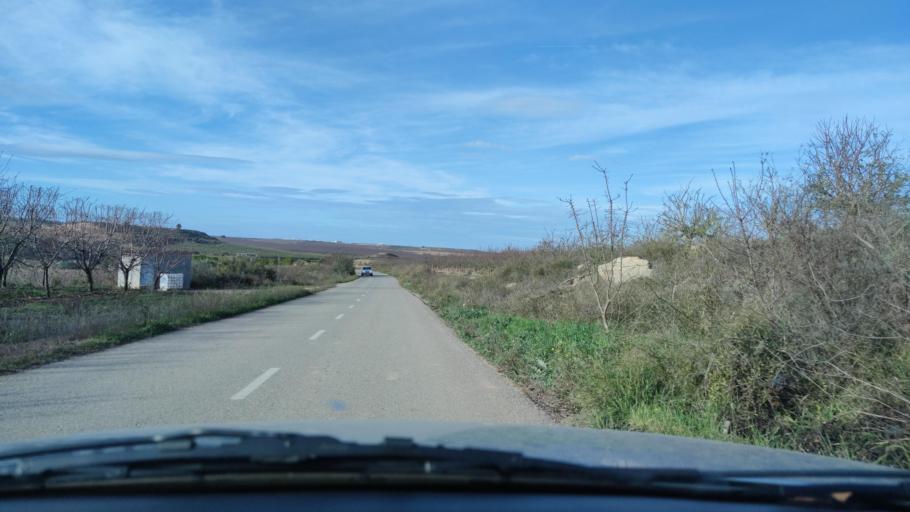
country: ES
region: Catalonia
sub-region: Provincia de Lleida
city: Alcano
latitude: 41.4688
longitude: 0.6418
